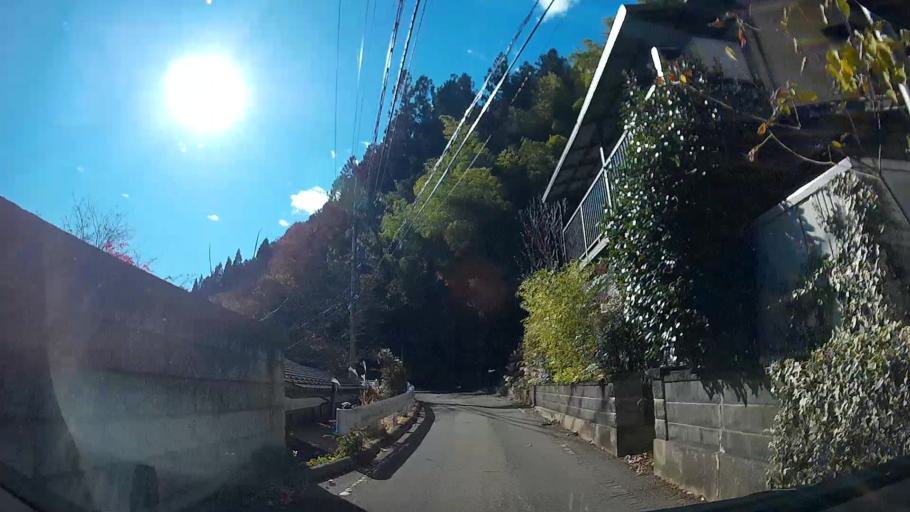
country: JP
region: Yamanashi
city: Otsuki
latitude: 35.6379
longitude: 138.9531
